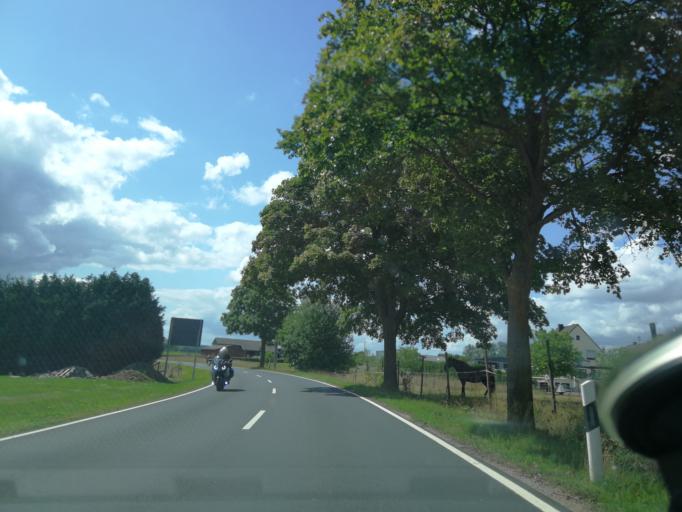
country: DE
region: Rheinland-Pfalz
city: Herforst
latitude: 49.9646
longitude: 6.7002
